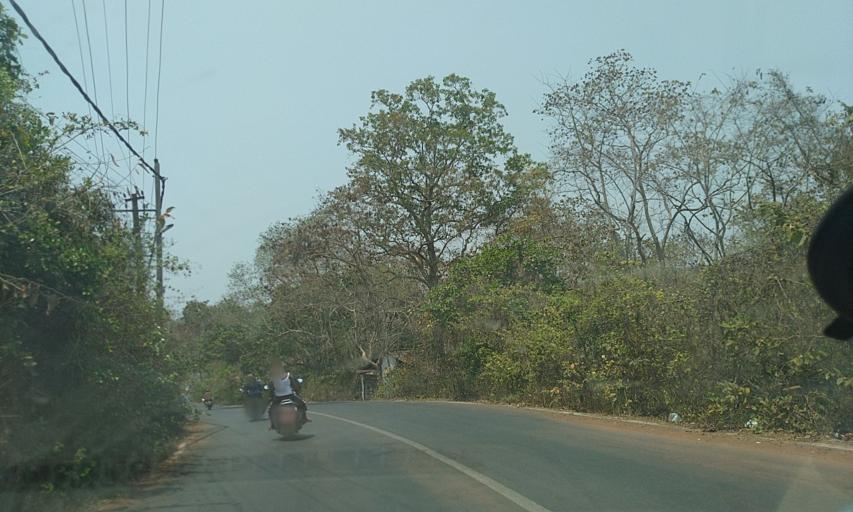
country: IN
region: Goa
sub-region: North Goa
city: Mapuca
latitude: 15.5966
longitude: 73.7933
